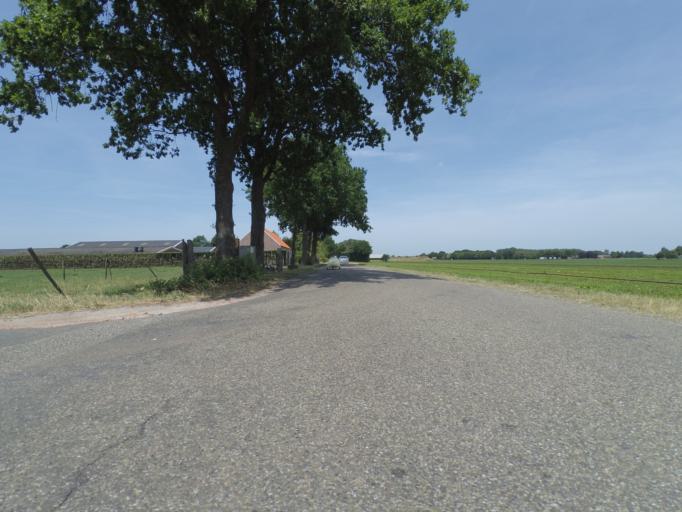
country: NL
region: North Brabant
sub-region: Gemeente Steenbergen
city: Welberg
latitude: 51.5233
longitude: 4.3498
